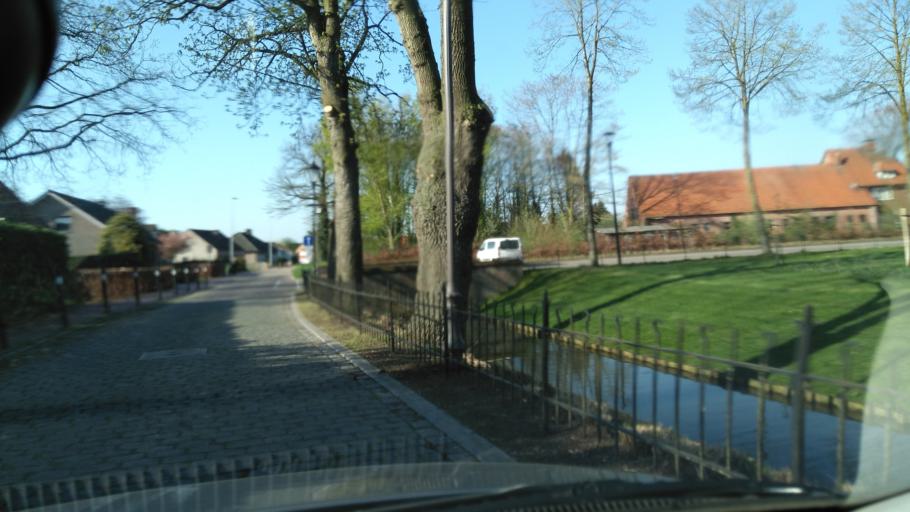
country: BE
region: Flanders
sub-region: Provincie Antwerpen
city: Ravels
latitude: 51.4081
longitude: 4.9964
